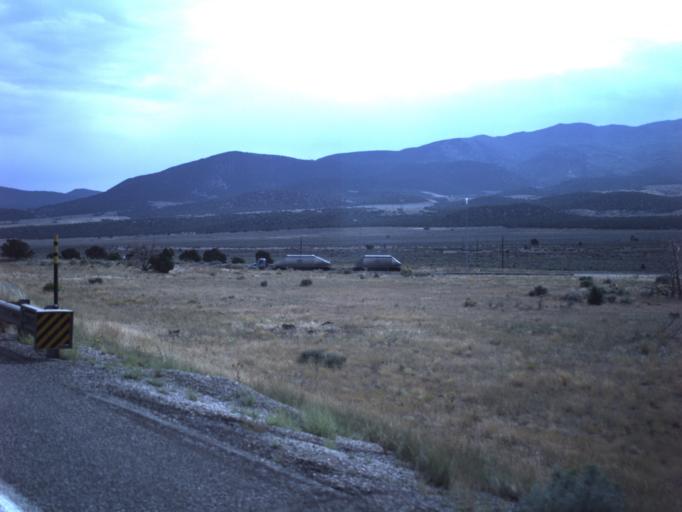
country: US
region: Utah
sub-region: Beaver County
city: Beaver
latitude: 38.5762
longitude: -112.6053
